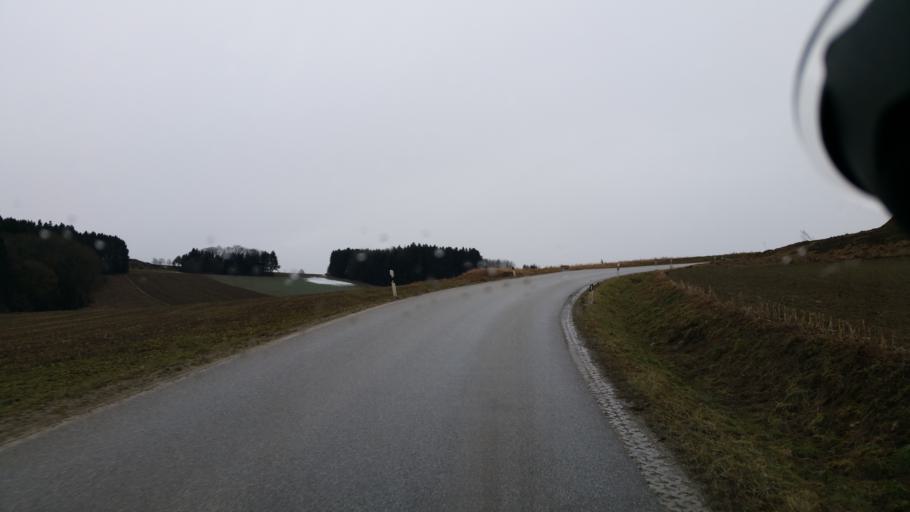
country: DE
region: Bavaria
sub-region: Lower Bavaria
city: Eching
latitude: 48.4946
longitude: 12.0718
